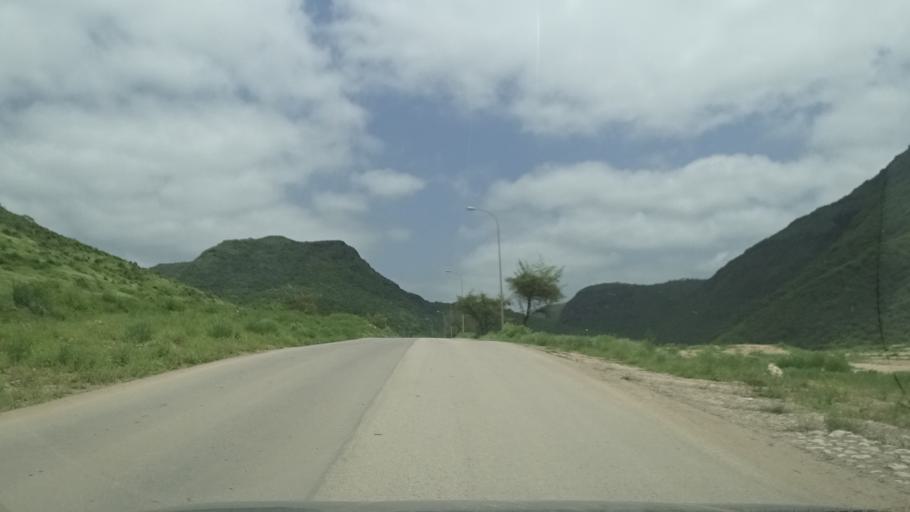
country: OM
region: Zufar
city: Salalah
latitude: 17.1460
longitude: 54.1759
